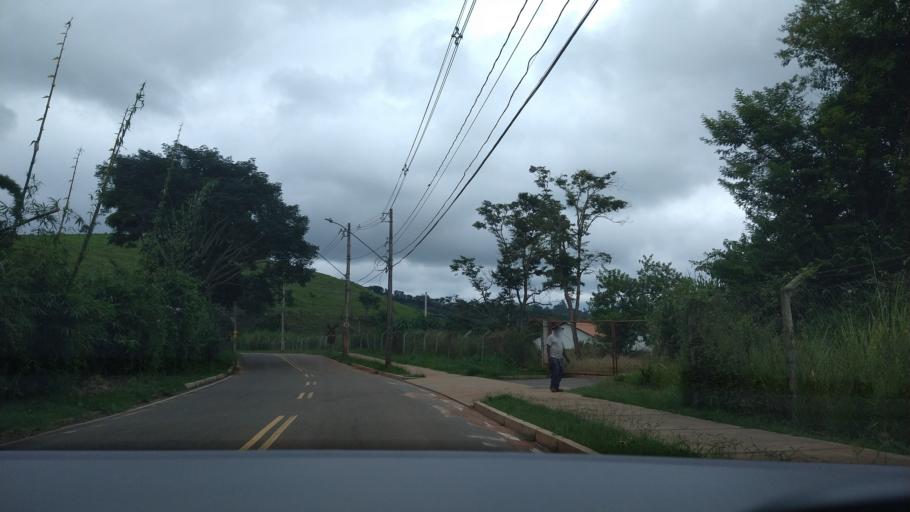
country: BR
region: Minas Gerais
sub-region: Vicosa
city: Vicosa
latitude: -20.7679
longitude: -42.8575
